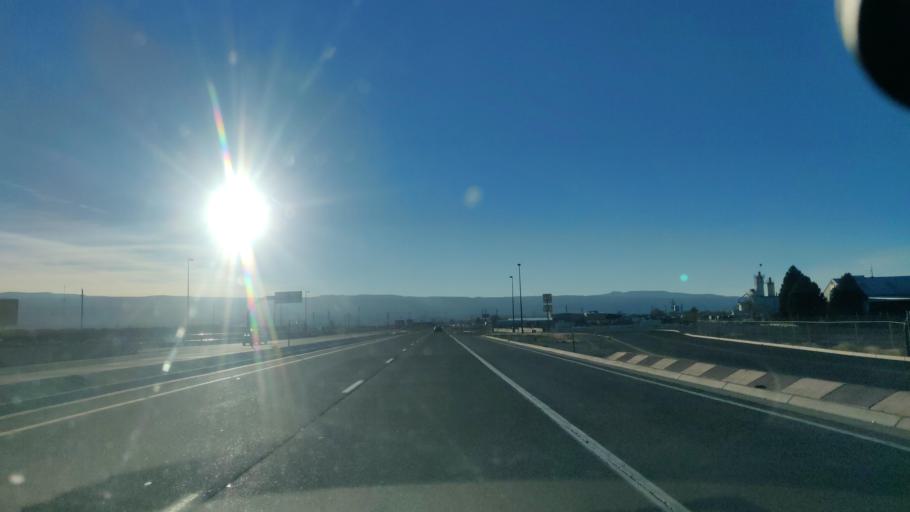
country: US
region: Colorado
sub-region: Mesa County
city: Fruitvale
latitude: 39.0830
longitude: -108.5087
